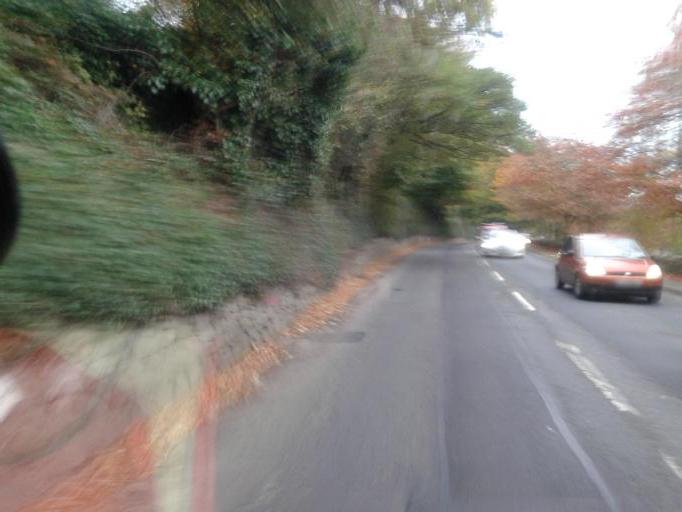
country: IE
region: Munster
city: Ballina
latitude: 52.8053
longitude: -8.4347
